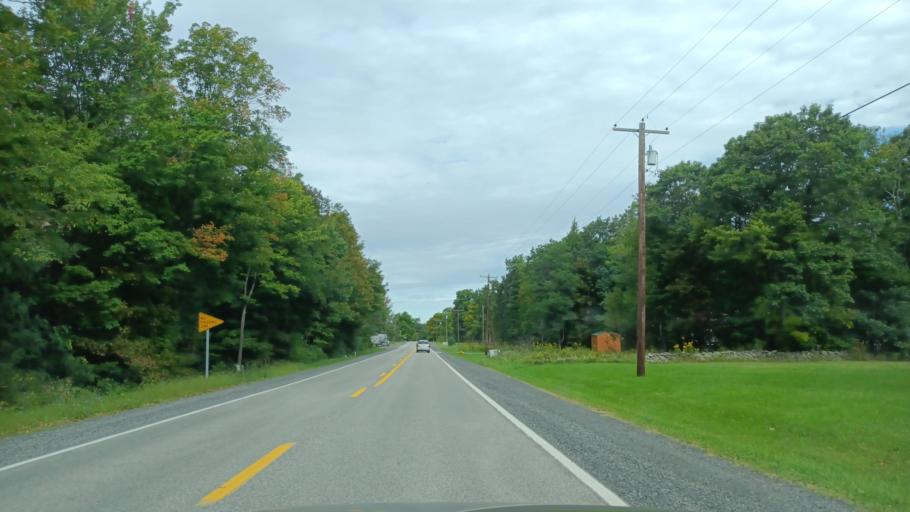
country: US
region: Maryland
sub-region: Garrett County
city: Mountain Lake Park
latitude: 39.2548
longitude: -79.2291
